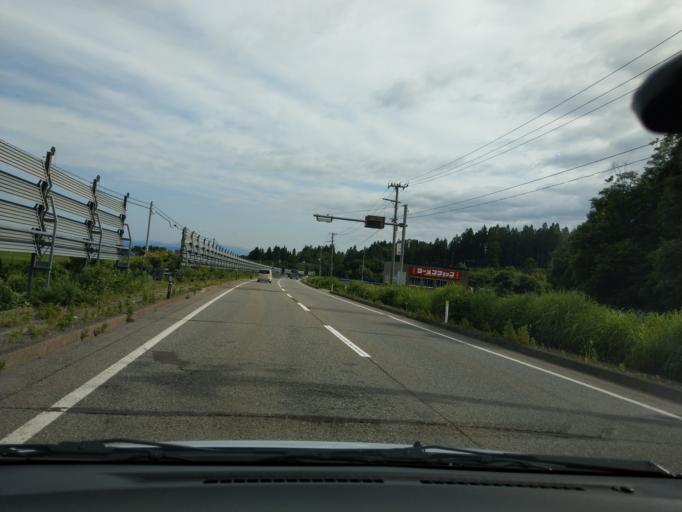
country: JP
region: Akita
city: Yokotemachi
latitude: 39.3844
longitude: 140.5678
